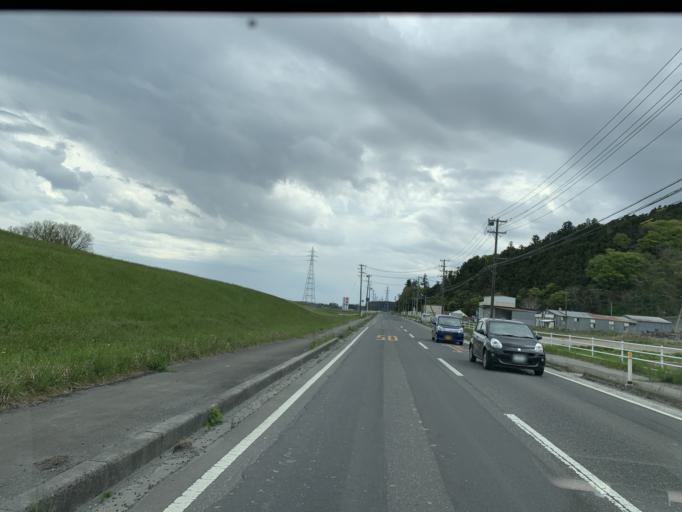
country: JP
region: Iwate
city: Ichinoseki
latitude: 38.7360
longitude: 141.2963
